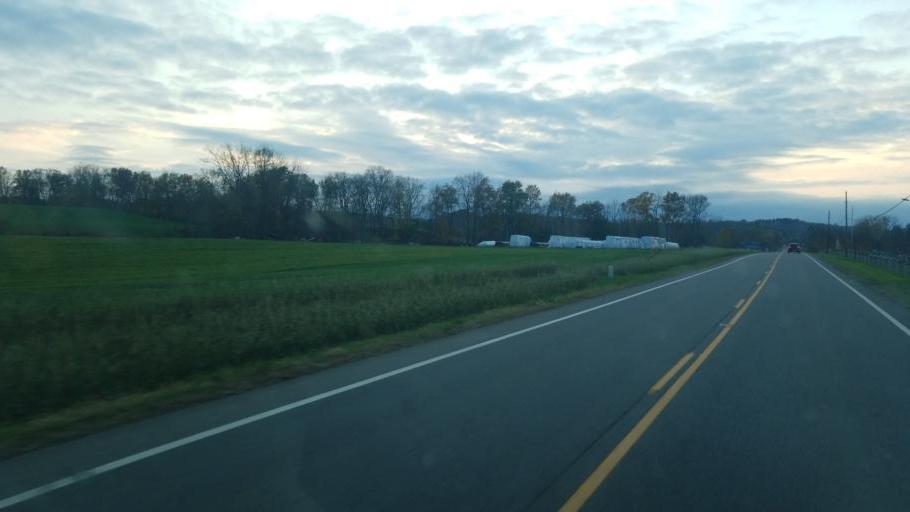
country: US
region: Ohio
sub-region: Ashland County
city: Loudonville
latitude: 40.6531
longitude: -82.2946
